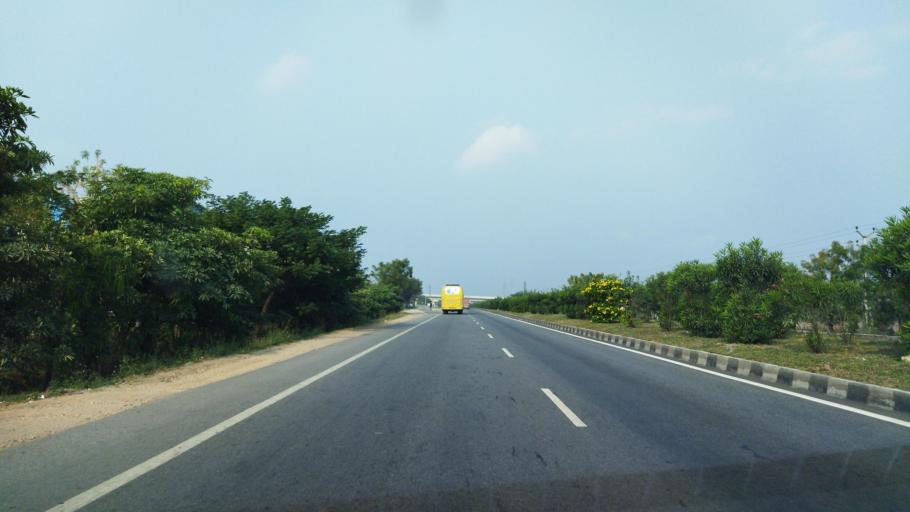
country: IN
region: Telangana
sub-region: Nalgonda
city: Nalgonda
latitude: 17.1682
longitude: 79.3997
